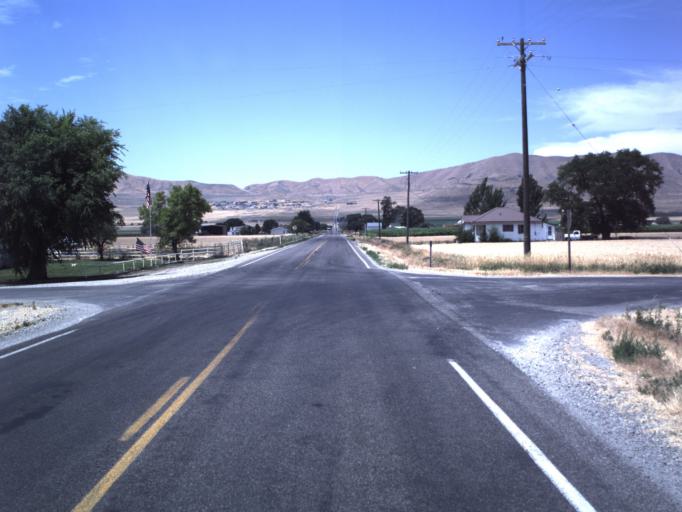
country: US
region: Utah
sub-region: Box Elder County
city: Tremonton
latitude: 41.7097
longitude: -112.2583
